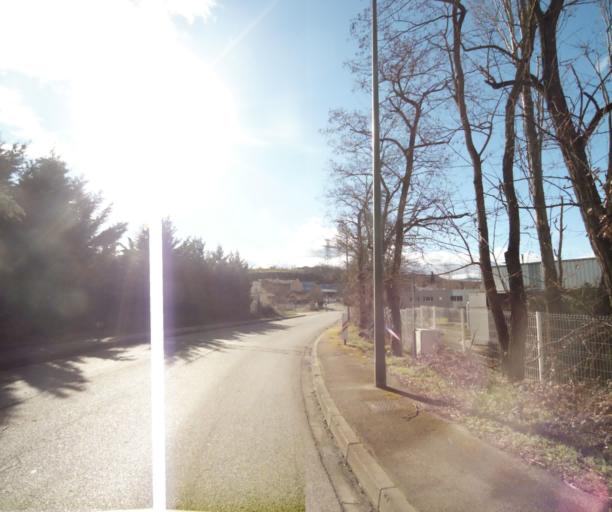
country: FR
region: Rhone-Alpes
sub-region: Departement de la Loire
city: La Talaudiere
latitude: 45.4627
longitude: 4.4248
